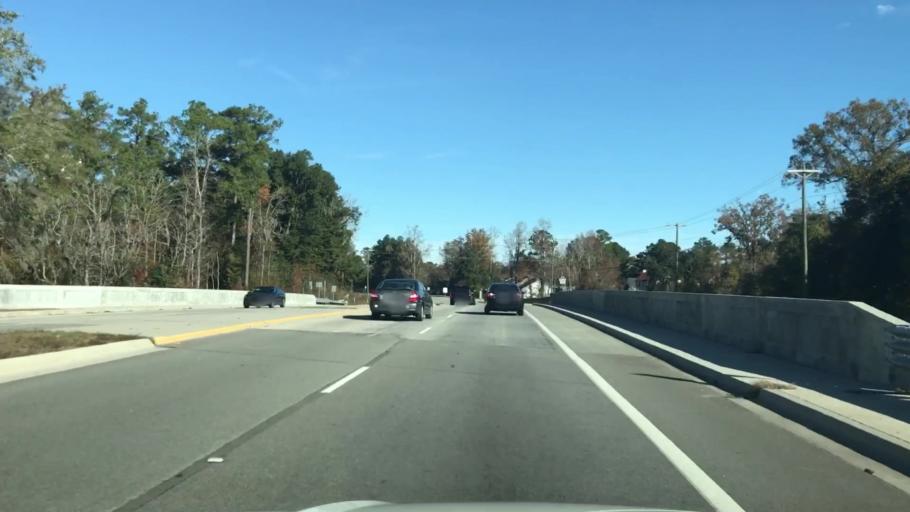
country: US
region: South Carolina
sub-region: Dorchester County
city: Centerville
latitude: 32.9579
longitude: -80.2009
